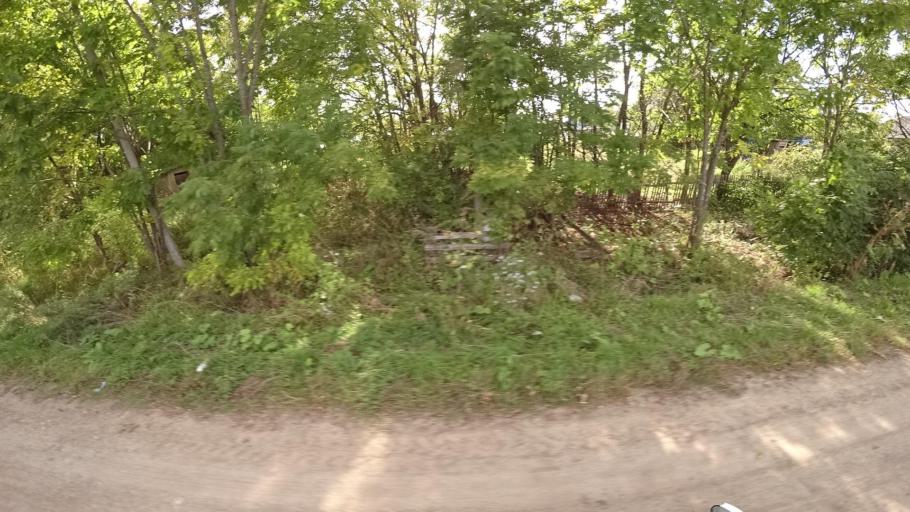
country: RU
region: Primorskiy
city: Dostoyevka
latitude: 44.3010
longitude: 133.4591
